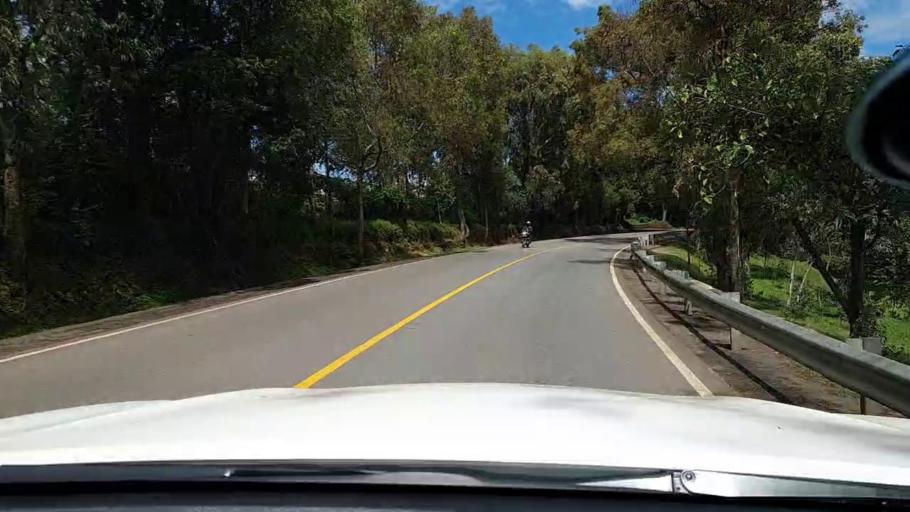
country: RW
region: Kigali
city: Kigali
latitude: -1.8235
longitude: 29.9426
